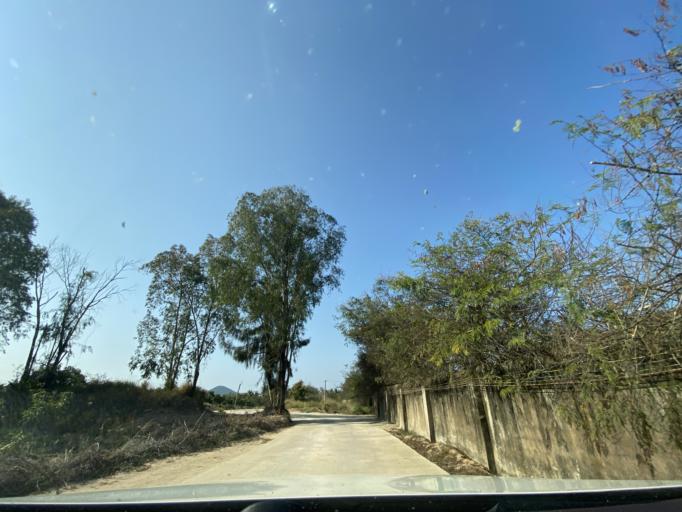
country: CN
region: Hainan
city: Haitangwan
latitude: 18.3995
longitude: 109.7677
